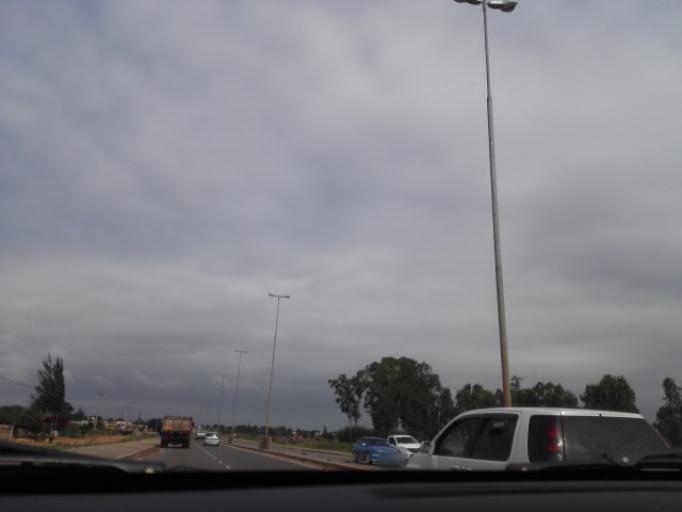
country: MZ
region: Maputo City
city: Maputo
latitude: -25.8288
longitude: 32.6094
